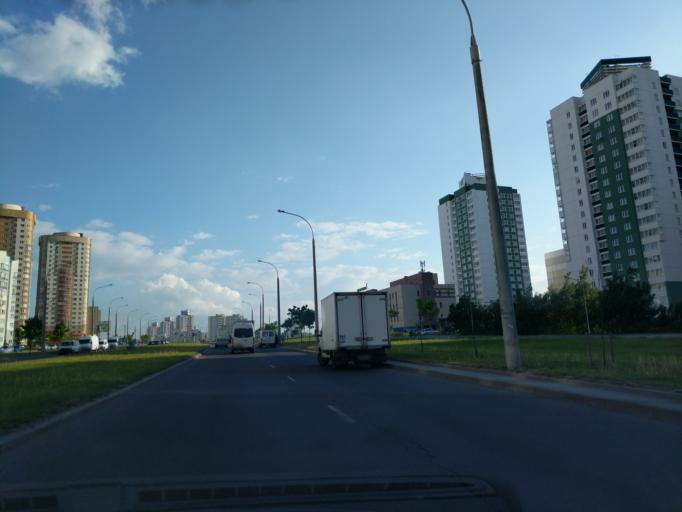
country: BY
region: Minsk
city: Zhdanovichy
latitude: 53.9227
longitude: 27.4389
